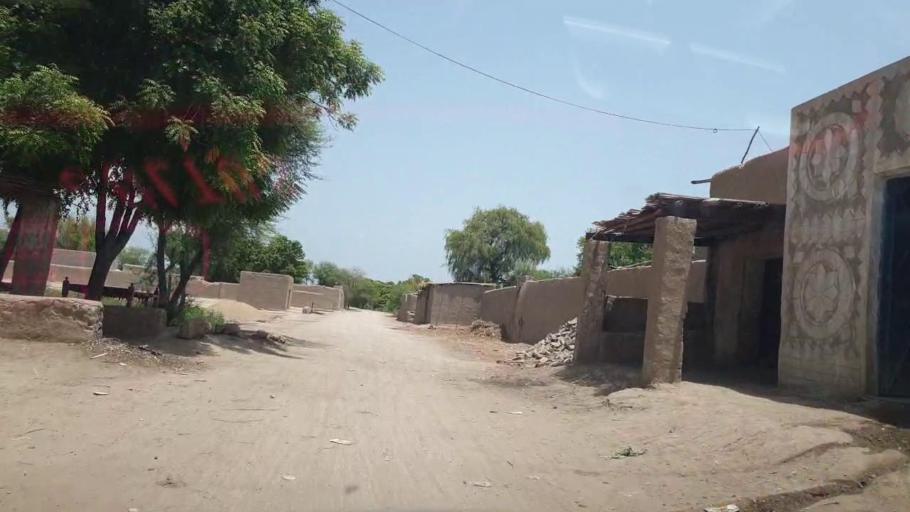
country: PK
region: Sindh
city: Daulatpur
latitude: 26.3895
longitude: 68.0650
